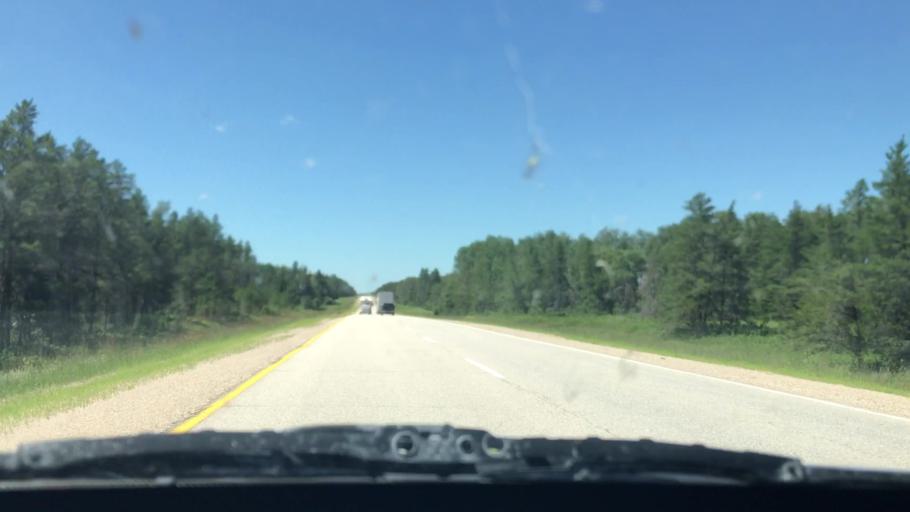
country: CA
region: Manitoba
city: La Broquerie
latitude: 49.6570
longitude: -96.1873
